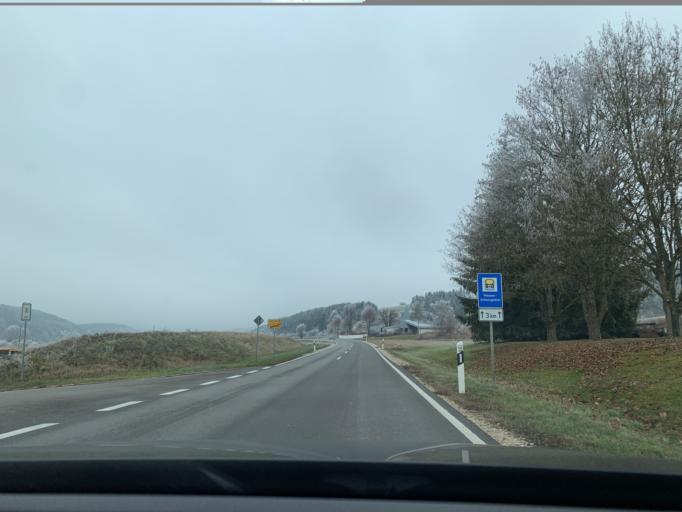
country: DE
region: Baden-Wuerttemberg
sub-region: Freiburg Region
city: Geisingen
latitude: 47.8879
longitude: 8.6620
